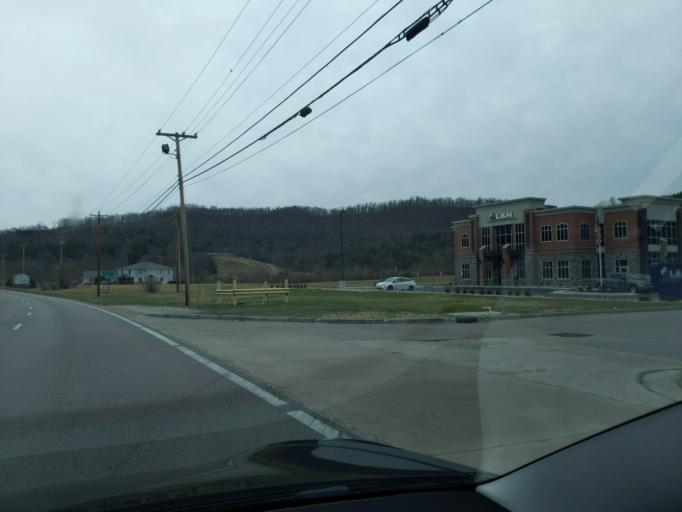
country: US
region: Kentucky
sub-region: Whitley County
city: Corbin
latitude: 36.9183
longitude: -84.1216
